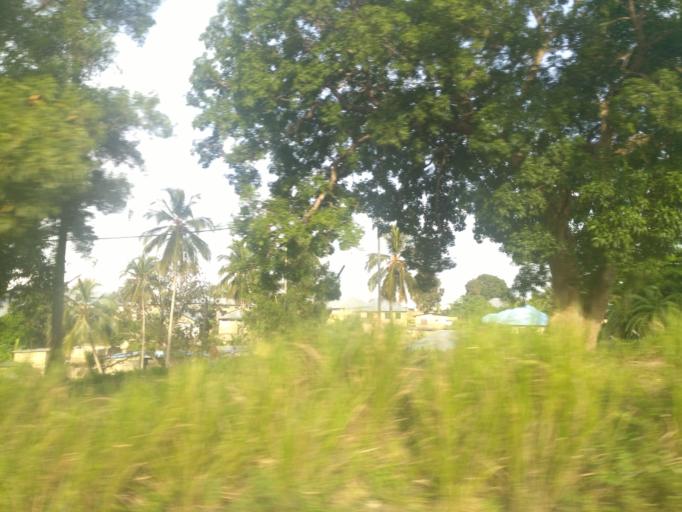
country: TZ
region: Zanzibar Urban/West
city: Zanzibar
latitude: -6.1552
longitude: 39.2349
